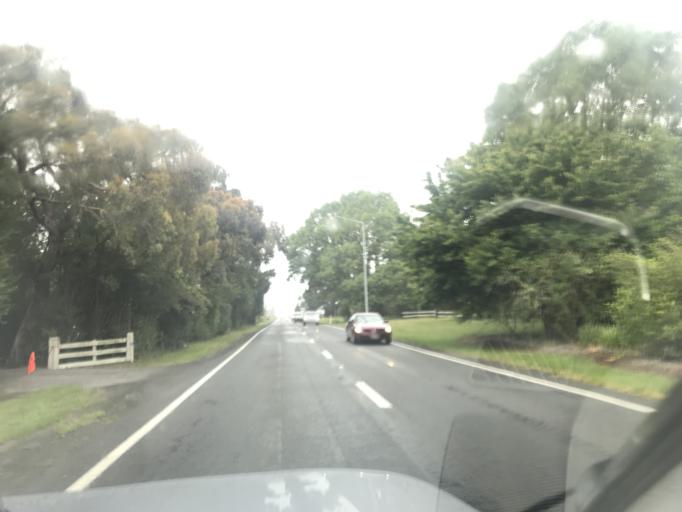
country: NZ
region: Canterbury
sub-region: Selwyn District
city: Darfield
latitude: -43.5014
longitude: 172.2176
